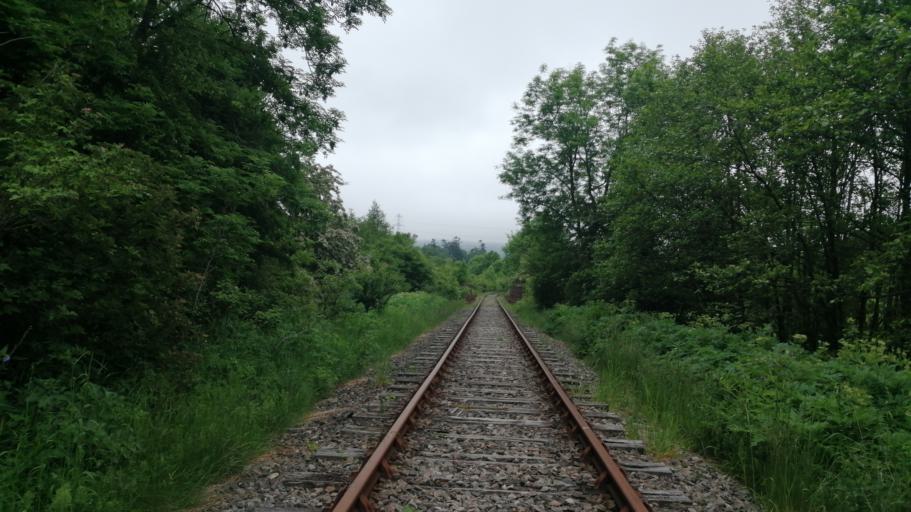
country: GB
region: Scotland
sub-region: Moray
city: Keith
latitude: 57.5376
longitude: -2.9612
